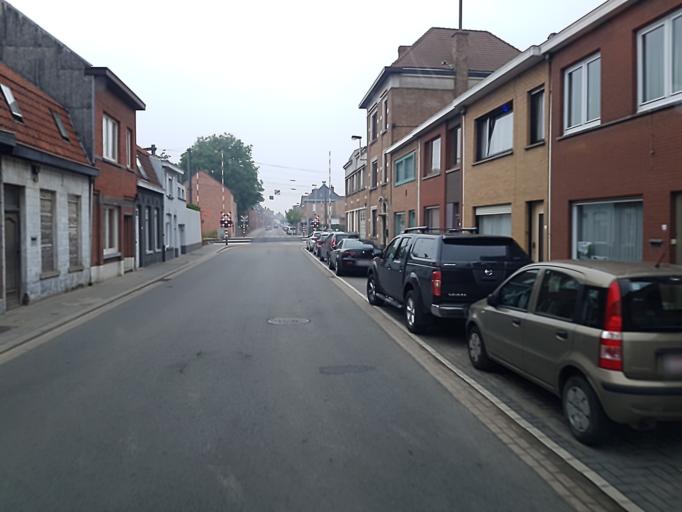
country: BE
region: Flanders
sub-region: Provincie West-Vlaanderen
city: Wervik
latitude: 50.7816
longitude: 3.0399
